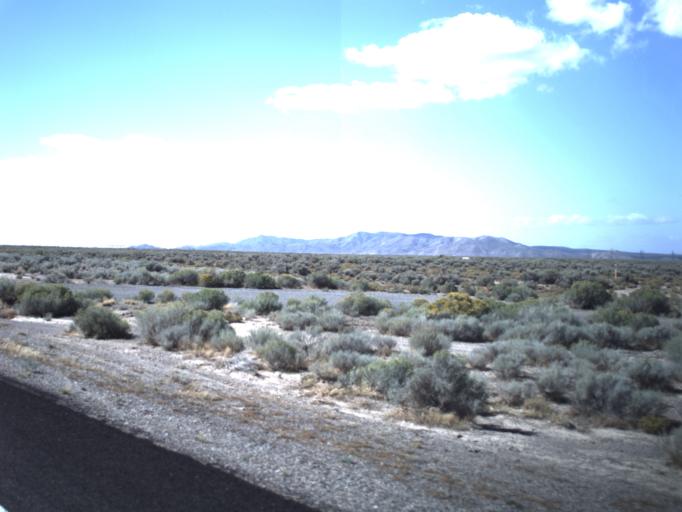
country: US
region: Utah
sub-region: Beaver County
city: Milford
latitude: 38.4451
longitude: -113.0092
